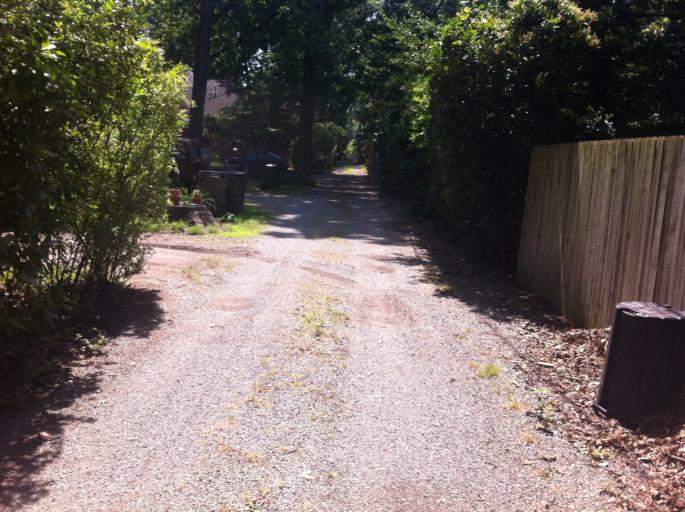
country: US
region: Virginia
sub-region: Henrico County
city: Dumbarton
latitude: 37.5739
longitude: -77.4949
